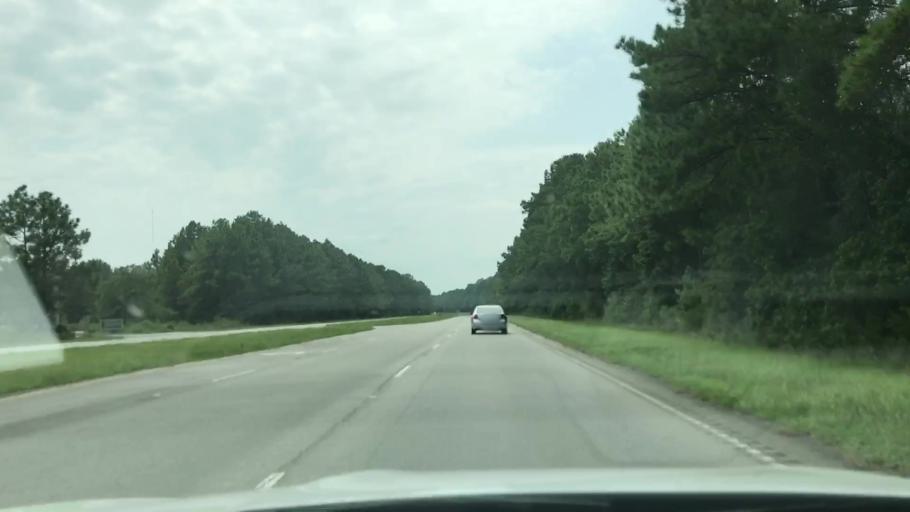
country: US
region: South Carolina
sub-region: Charleston County
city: Awendaw
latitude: 32.9757
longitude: -79.6689
